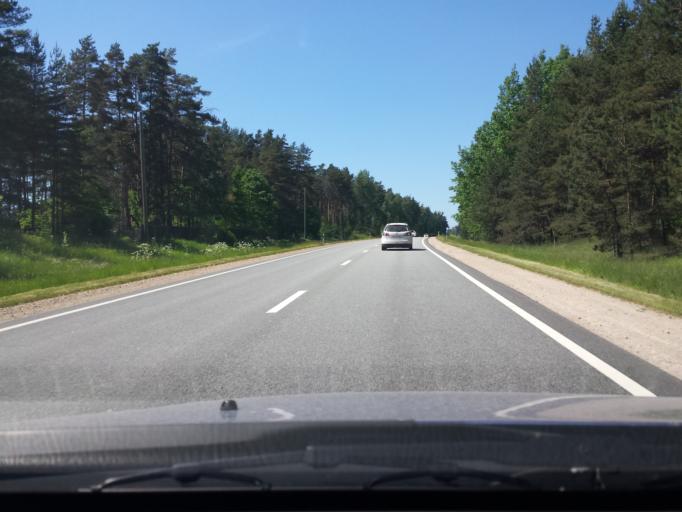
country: LV
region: Riga
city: Bergi
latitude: 56.9696
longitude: 24.3504
